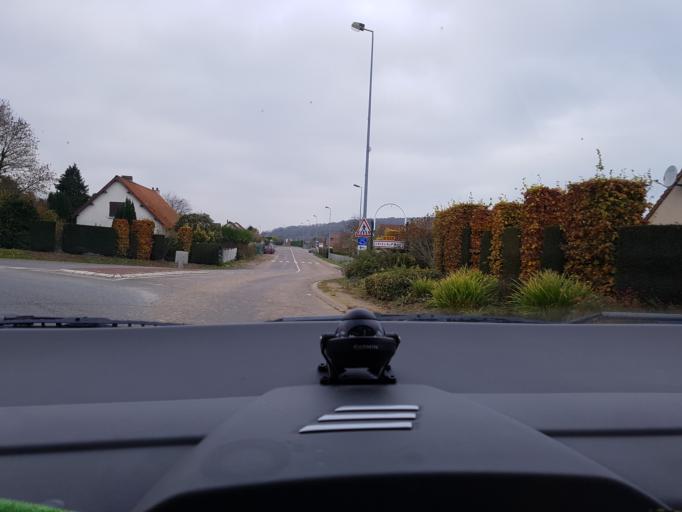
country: FR
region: Haute-Normandie
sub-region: Departement de la Seine-Maritime
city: Criel-sur-Mer
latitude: 50.0215
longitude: 1.3239
